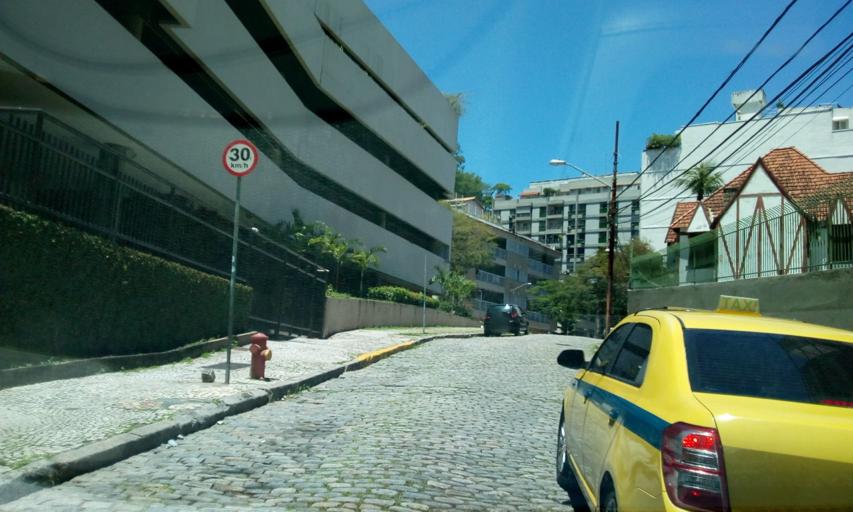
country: BR
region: Rio de Janeiro
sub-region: Rio De Janeiro
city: Rio de Janeiro
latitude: -22.9376
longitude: -43.1811
